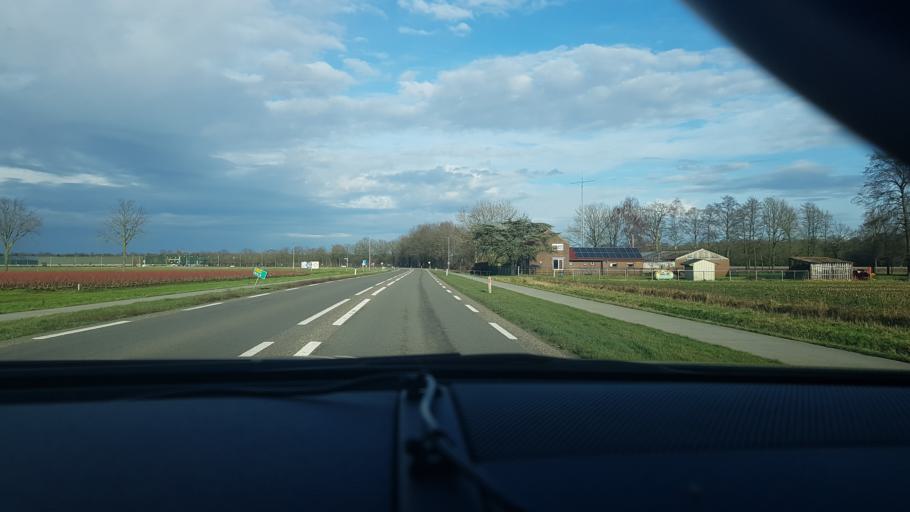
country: NL
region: Limburg
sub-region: Gemeente Venray
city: Venray
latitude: 51.4438
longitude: 5.9511
